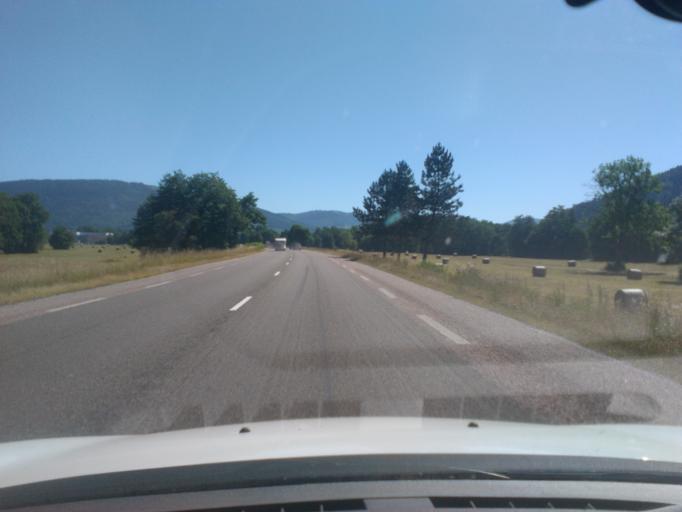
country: FR
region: Lorraine
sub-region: Departement des Vosges
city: Saint-Ame
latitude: 48.0144
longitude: 6.6586
